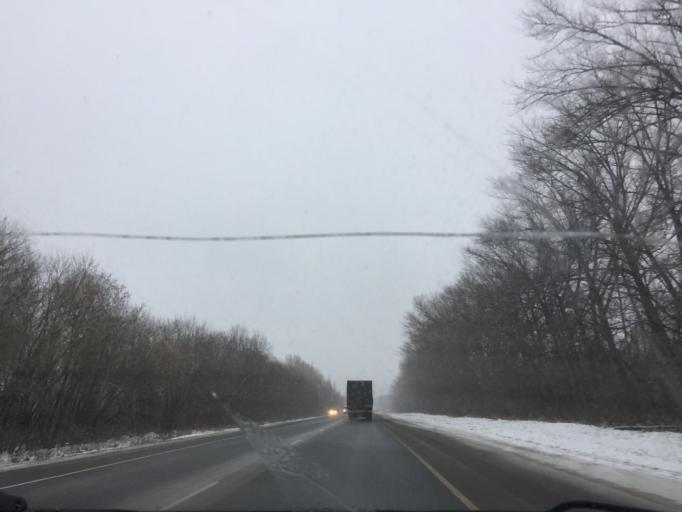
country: RU
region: Tula
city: Plavsk
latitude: 53.7563
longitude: 37.3335
